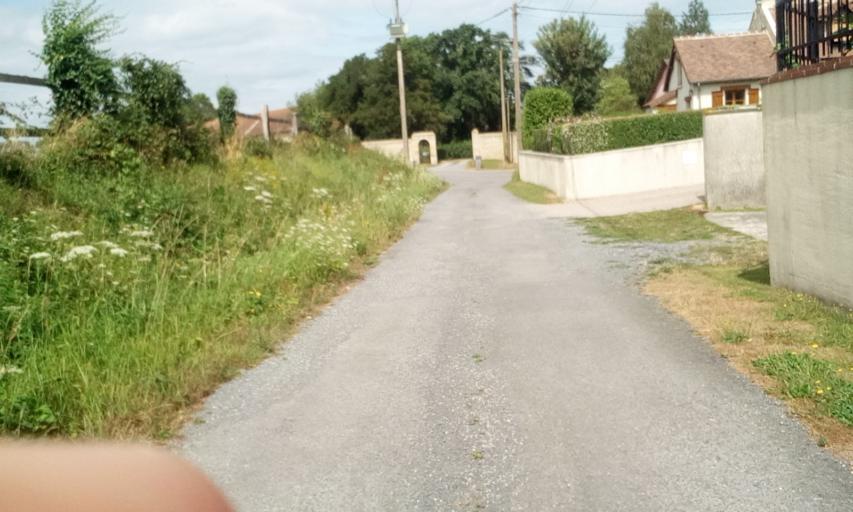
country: FR
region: Lower Normandy
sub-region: Departement du Calvados
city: Merville-Franceville-Plage
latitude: 49.2491
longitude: -0.2071
